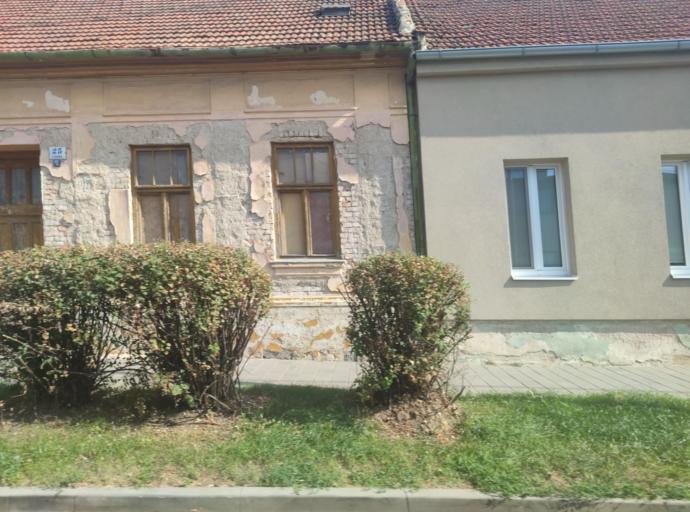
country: CZ
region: South Moravian
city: Podoli
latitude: 49.1753
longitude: 16.6862
